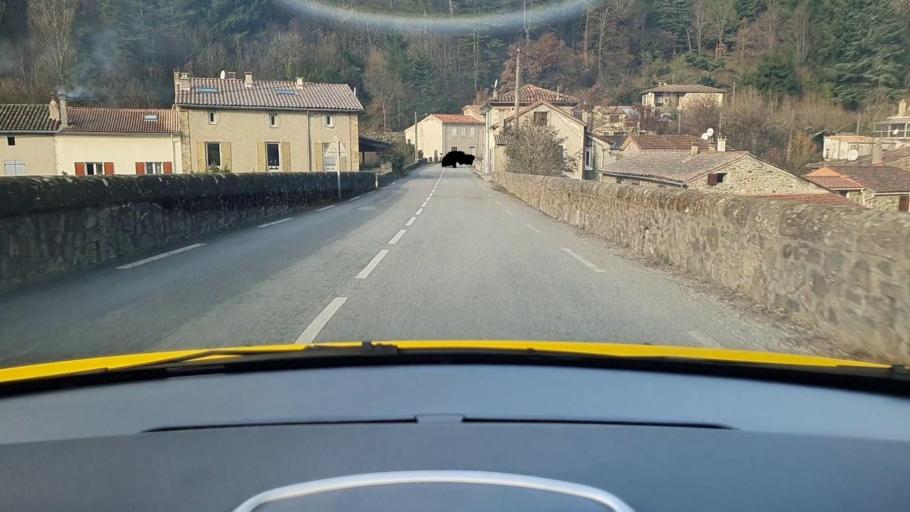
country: FR
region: Languedoc-Roussillon
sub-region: Departement du Gard
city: Branoux-les-Taillades
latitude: 44.3008
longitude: 3.9777
